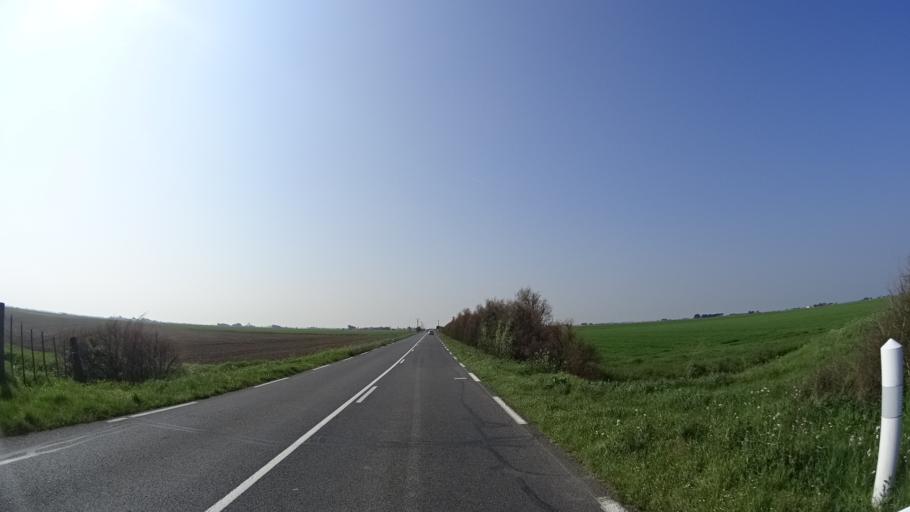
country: FR
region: Pays de la Loire
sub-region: Departement de la Loire-Atlantique
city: Bourgneuf-en-Retz
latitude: 47.0121
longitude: -1.9609
